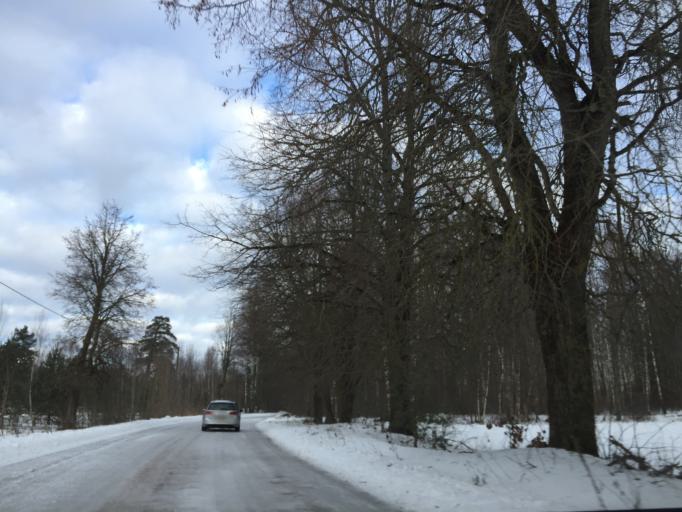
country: LV
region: Lielvarde
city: Lielvarde
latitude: 56.5725
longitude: 24.7342
